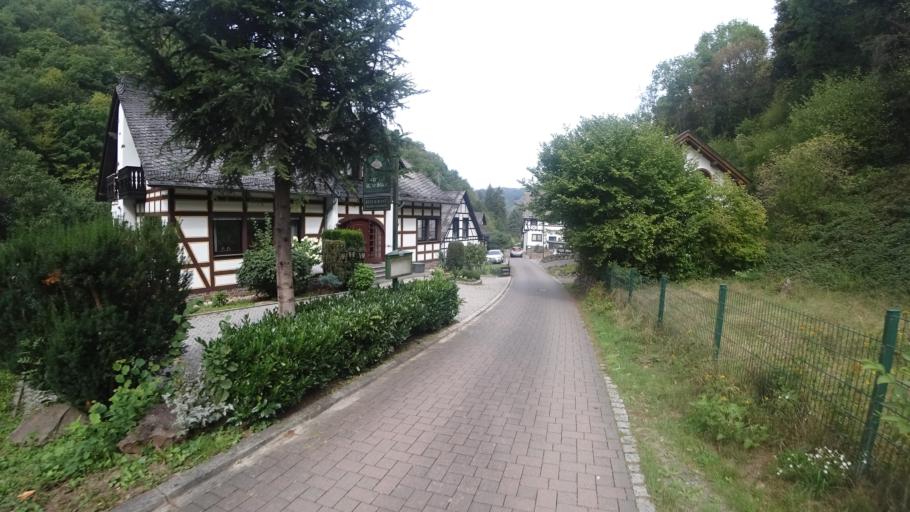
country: DE
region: Rheinland-Pfalz
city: Brodenbach
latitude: 50.2127
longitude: 7.4525
